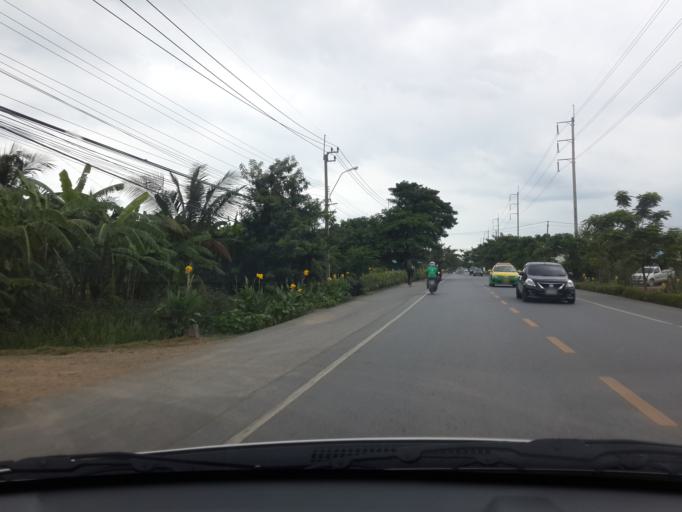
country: TH
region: Bangkok
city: Khlong Sam Wa
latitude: 13.8360
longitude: 100.7685
